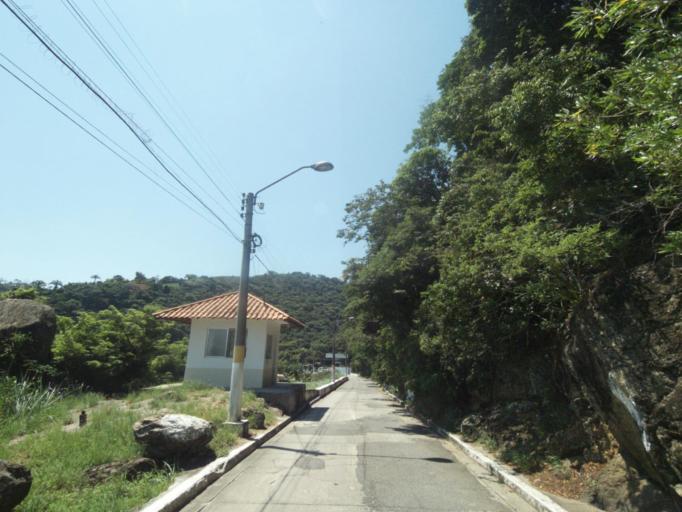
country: BR
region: Rio de Janeiro
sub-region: Niteroi
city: Niteroi
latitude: -22.9306
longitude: -43.1236
